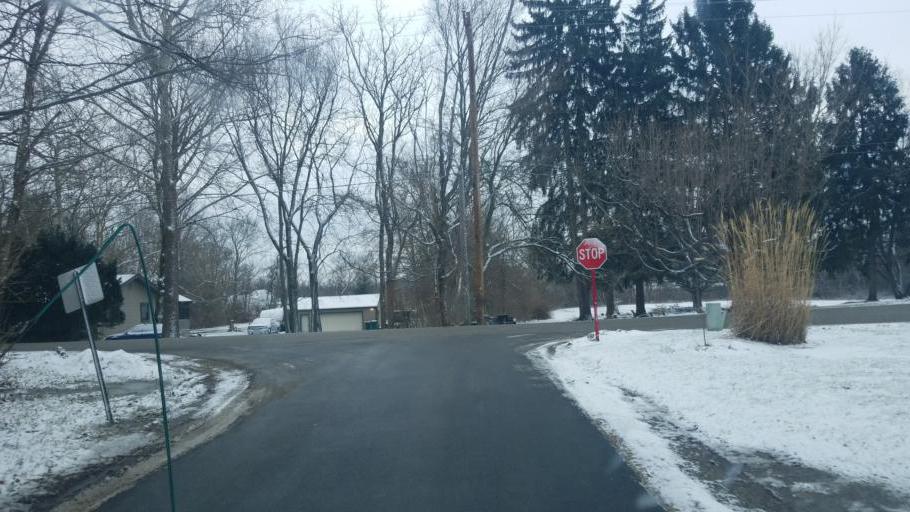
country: US
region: Ohio
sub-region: Franklin County
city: New Albany
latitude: 40.0303
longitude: -82.8175
